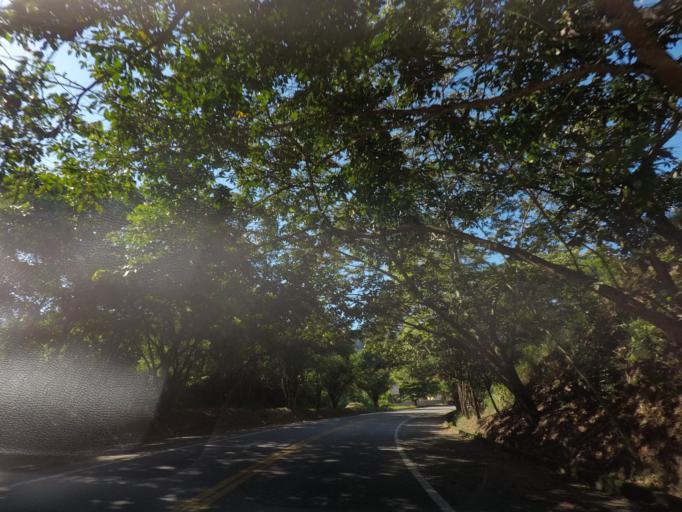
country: BR
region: Rio de Janeiro
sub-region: Parati
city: Paraty
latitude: -23.2688
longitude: -44.6824
